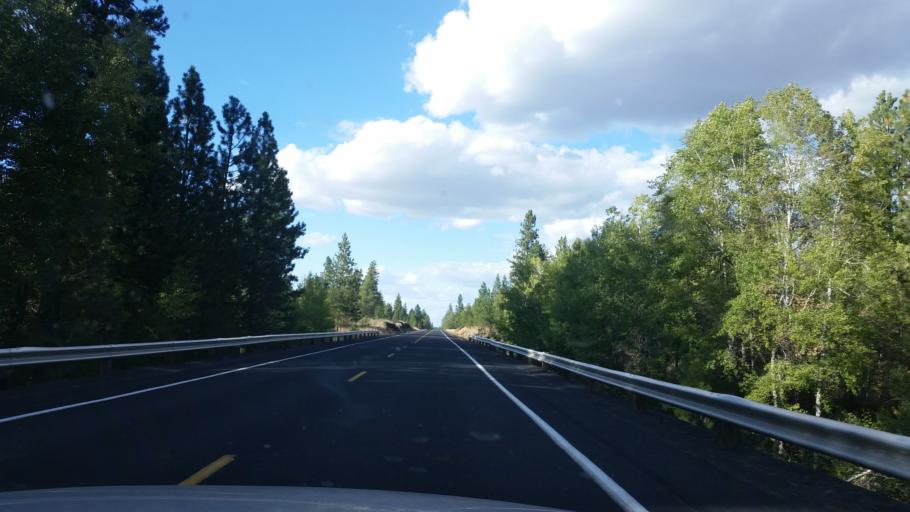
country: US
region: Washington
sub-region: Spokane County
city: Cheney
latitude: 47.4042
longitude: -117.5704
